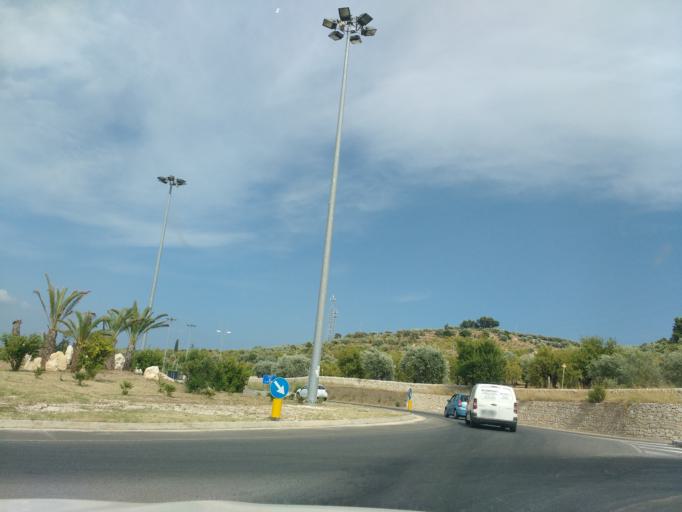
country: IT
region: Sicily
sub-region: Provincia di Siracusa
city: Noto
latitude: 36.8756
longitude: 15.0827
